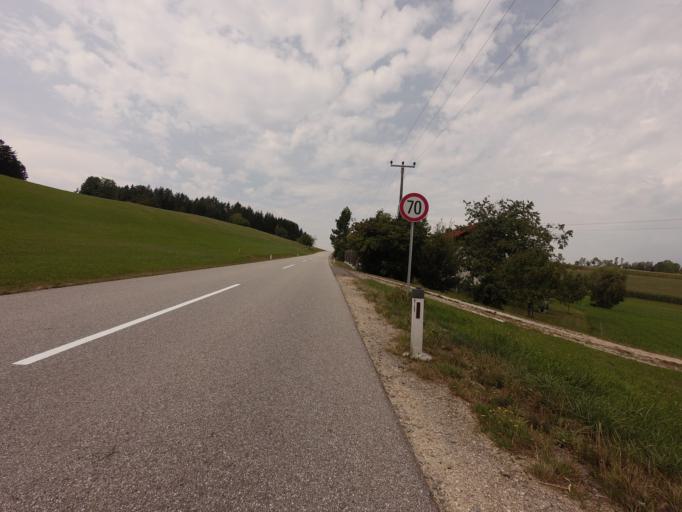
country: AT
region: Upper Austria
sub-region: Politischer Bezirk Urfahr-Umgebung
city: Reichenthal
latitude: 48.5552
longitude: 14.4150
